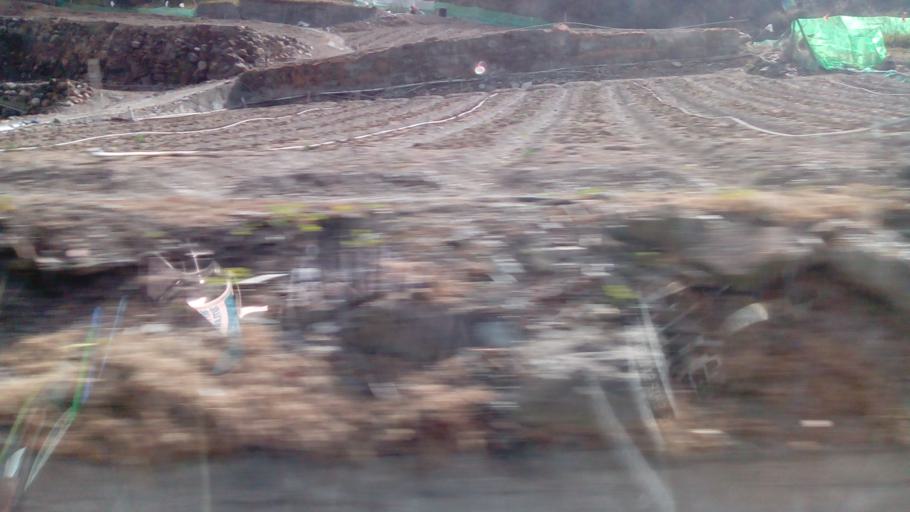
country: TW
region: Taiwan
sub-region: Hualien
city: Hualian
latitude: 24.3610
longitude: 121.3312
